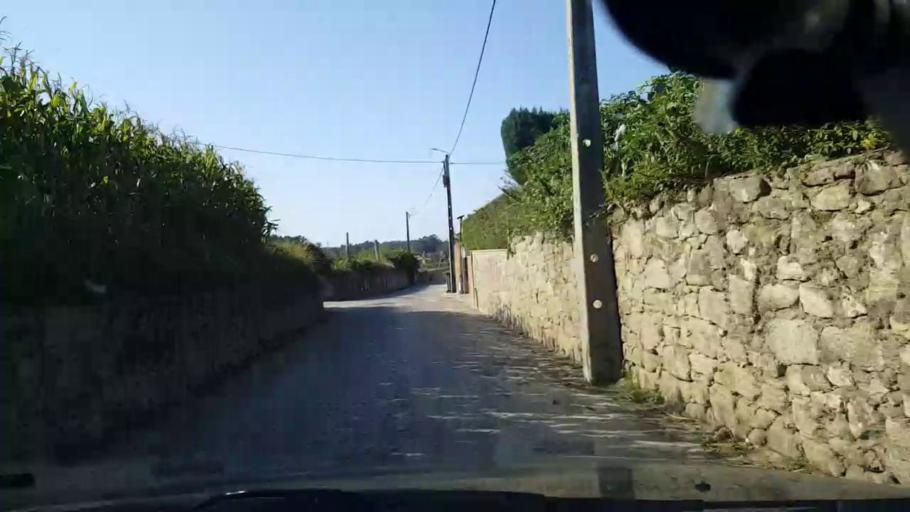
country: PT
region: Porto
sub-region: Vila do Conde
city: Arvore
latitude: 41.3576
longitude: -8.7189
